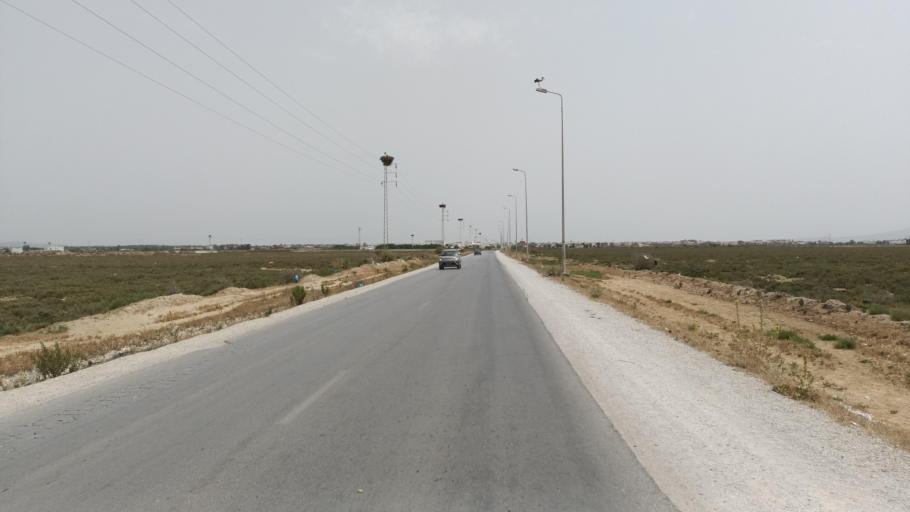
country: TN
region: Nabul
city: Manzil Bu Zalafah
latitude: 36.7185
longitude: 10.4762
